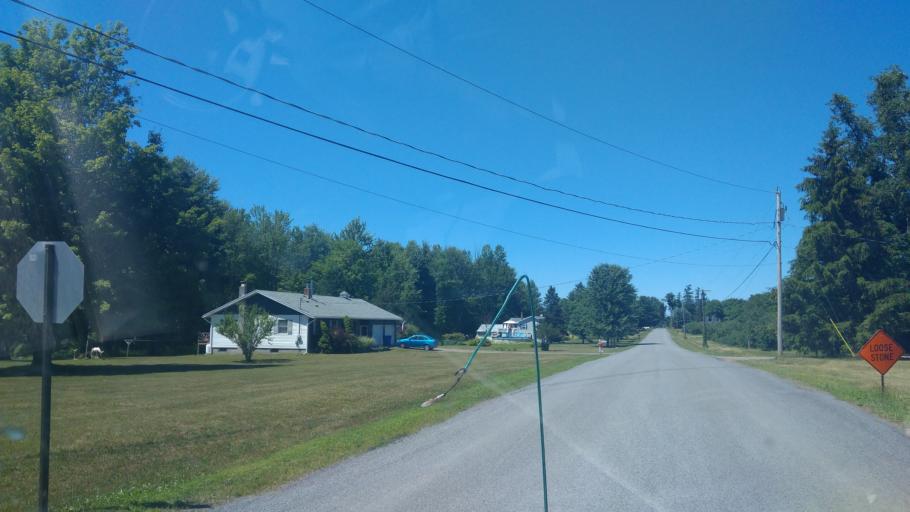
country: US
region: New York
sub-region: Wayne County
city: Lyons
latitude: 43.1674
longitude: -76.9771
